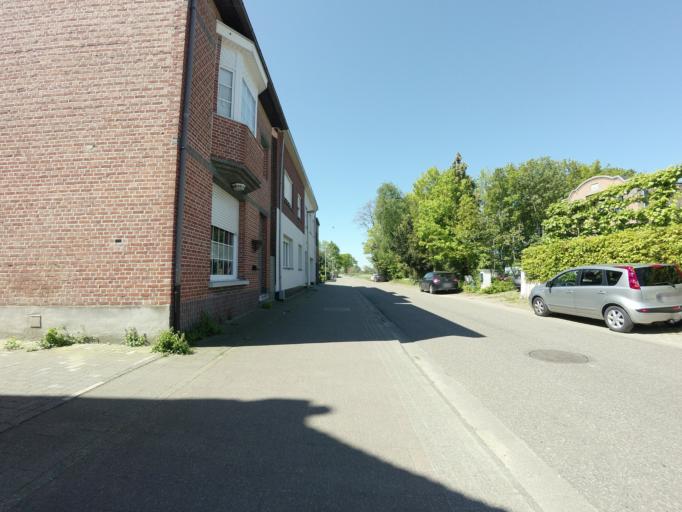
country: BE
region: Flanders
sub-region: Provincie Antwerpen
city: Essen
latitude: 51.4695
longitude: 4.4536
